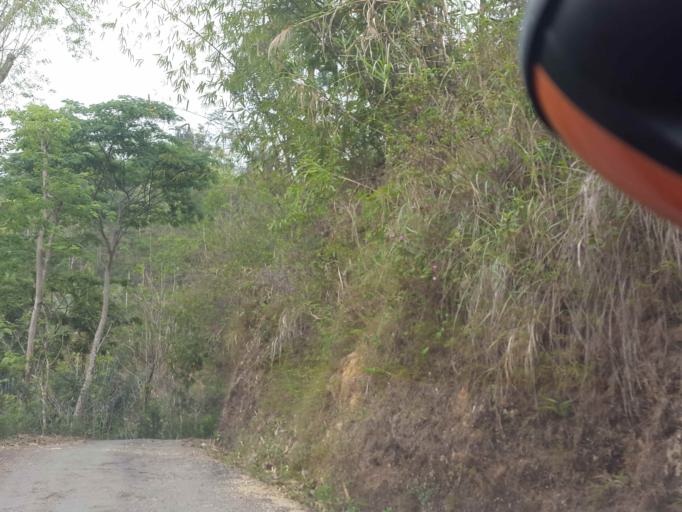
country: ID
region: East Java
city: Ploso
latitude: -8.0437
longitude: 111.1325
